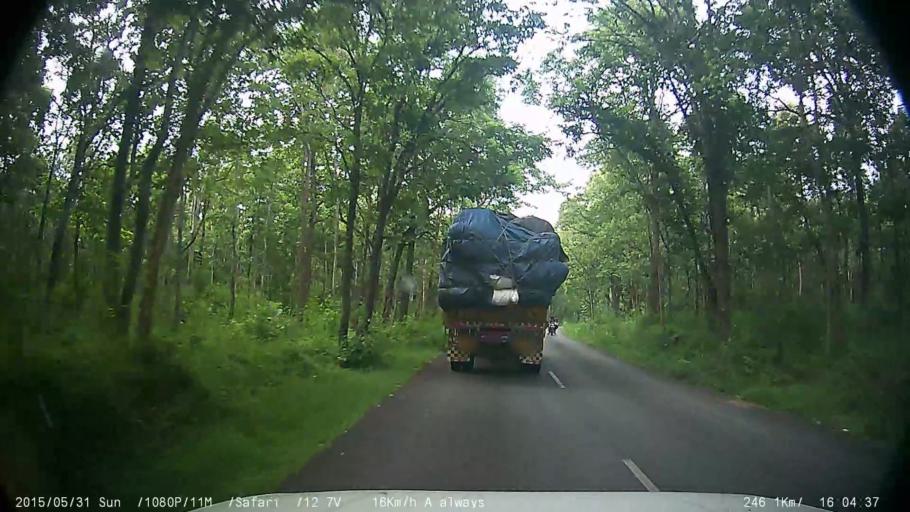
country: IN
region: Tamil Nadu
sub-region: Nilgiri
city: Naduvattam
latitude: 11.7107
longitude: 76.4165
